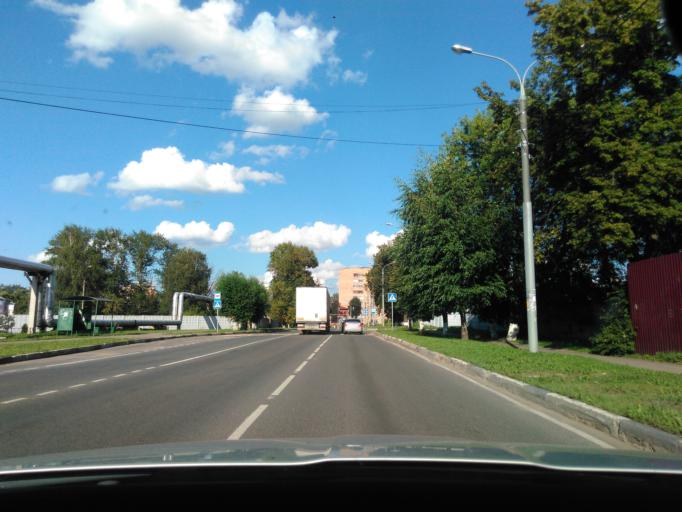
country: RU
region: Moskovskaya
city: Klin
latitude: 56.3344
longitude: 36.7187
